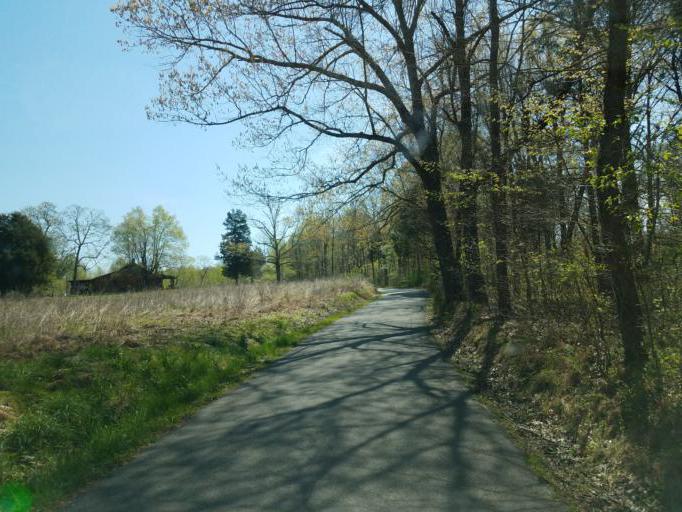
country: US
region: Kentucky
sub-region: Barren County
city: Cave City
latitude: 37.1768
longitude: -86.0468
